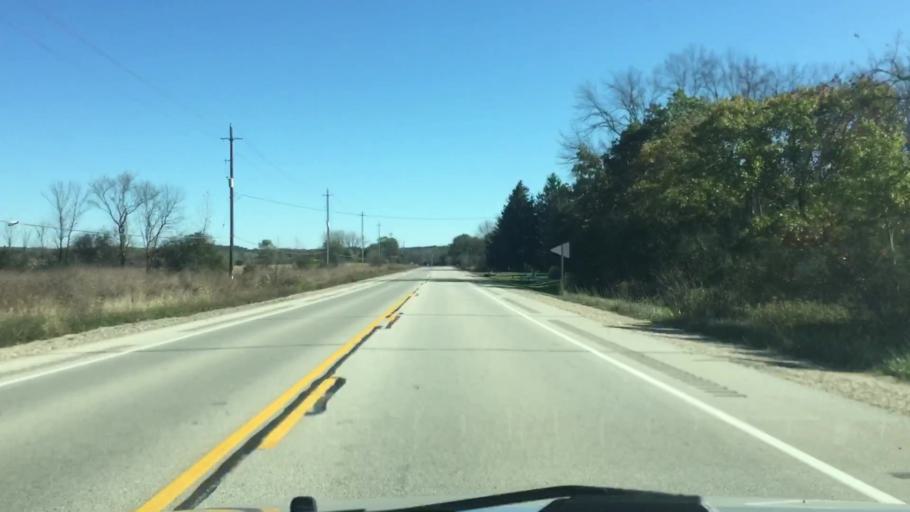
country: US
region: Wisconsin
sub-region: Waukesha County
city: Wales
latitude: 42.9591
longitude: -88.3495
